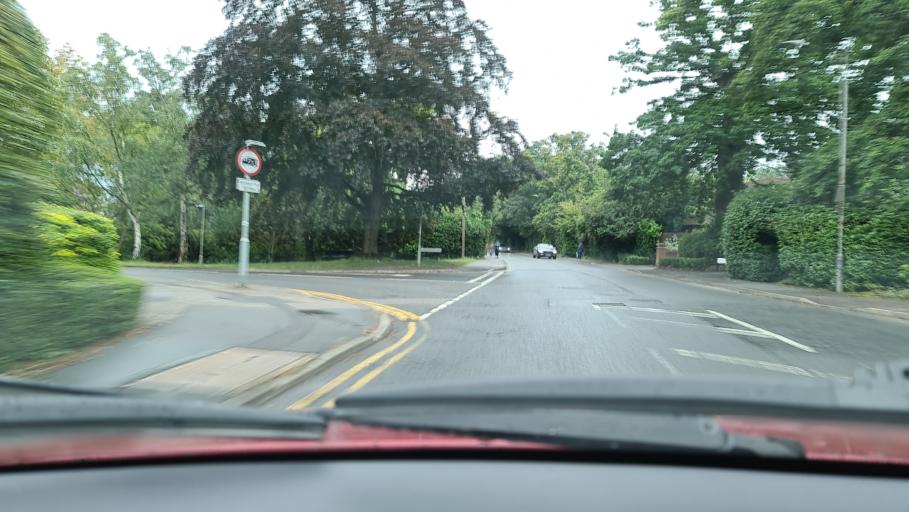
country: GB
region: England
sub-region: Buckinghamshire
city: Beaconsfield
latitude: 51.6070
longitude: -0.6411
